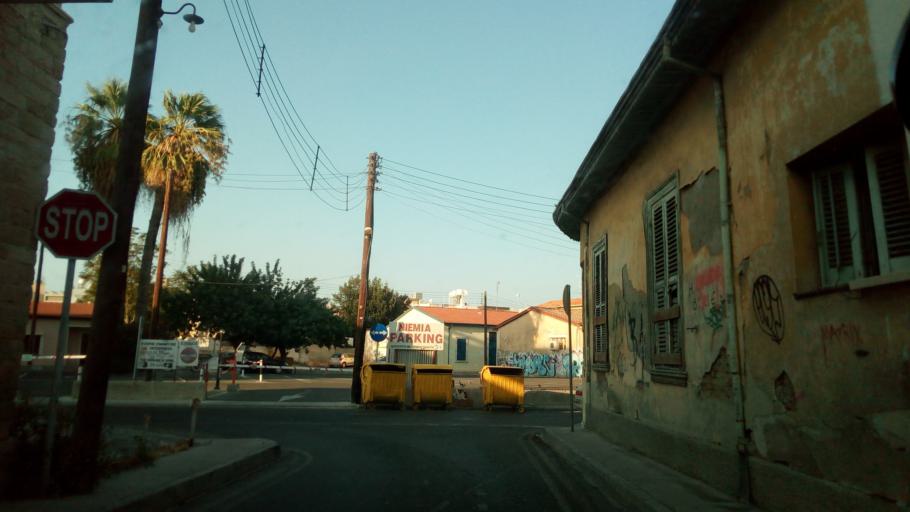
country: CY
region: Limassol
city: Limassol
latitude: 34.6791
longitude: 33.0468
